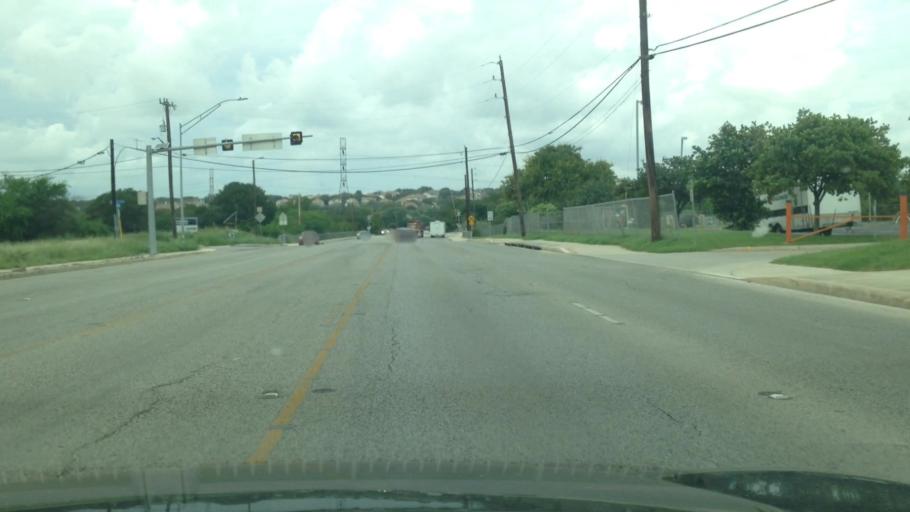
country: US
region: Texas
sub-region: Bexar County
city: Live Oak
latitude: 29.5829
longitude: -98.3941
